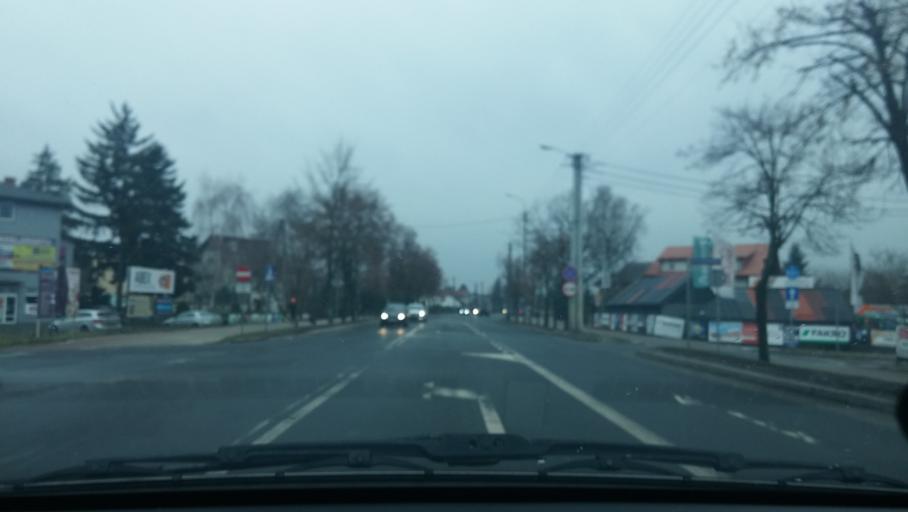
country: PL
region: Masovian Voivodeship
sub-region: Siedlce
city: Siedlce
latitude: 52.1671
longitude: 22.2553
